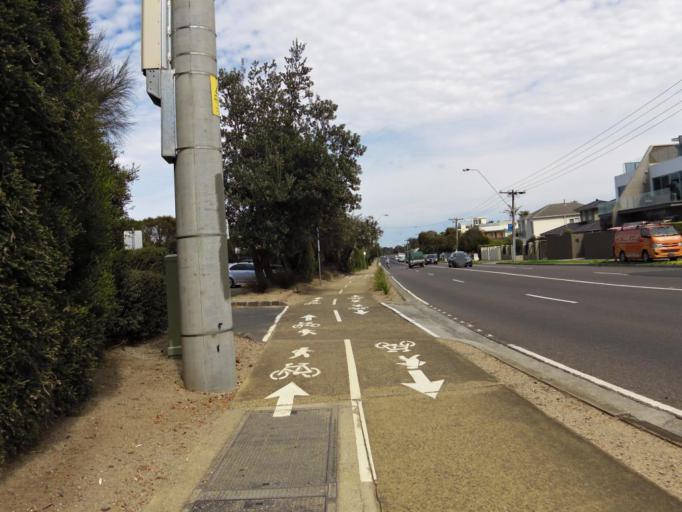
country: AU
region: Victoria
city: Beaumaris
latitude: -37.9925
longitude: 145.0418
